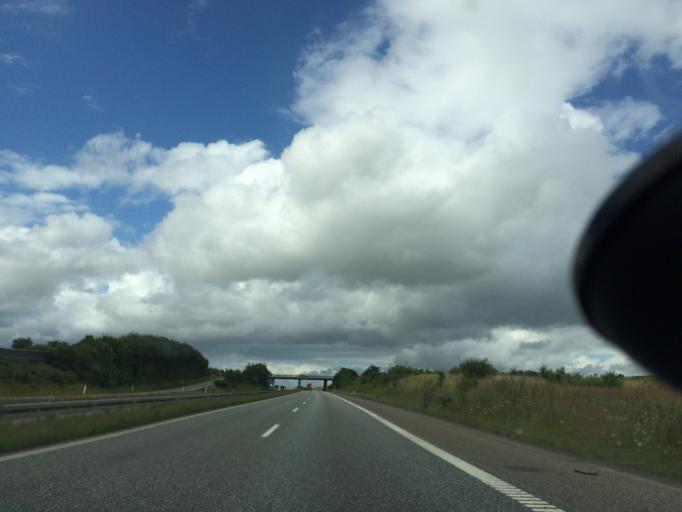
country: DK
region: Central Jutland
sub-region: Arhus Kommune
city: Framlev
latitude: 56.1534
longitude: 10.0120
